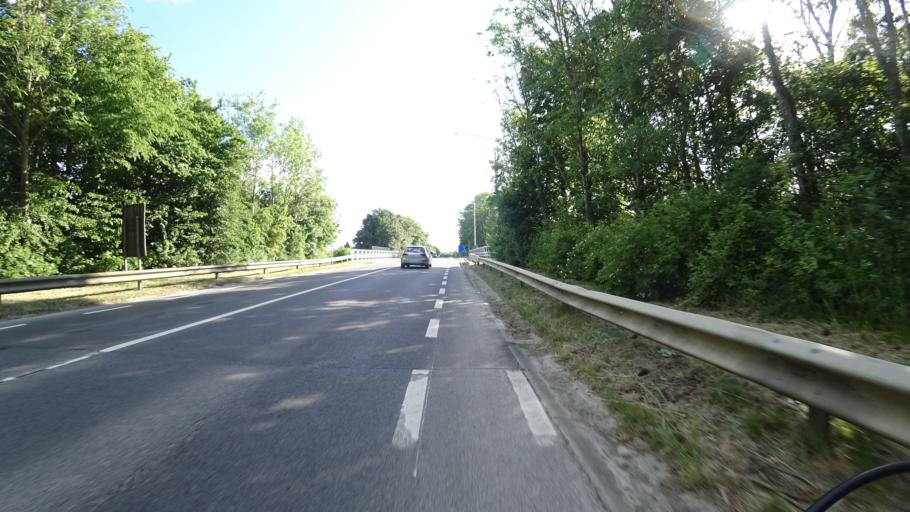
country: BE
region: Wallonia
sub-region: Province de Namur
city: Gembloux
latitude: 50.5208
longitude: 4.7699
